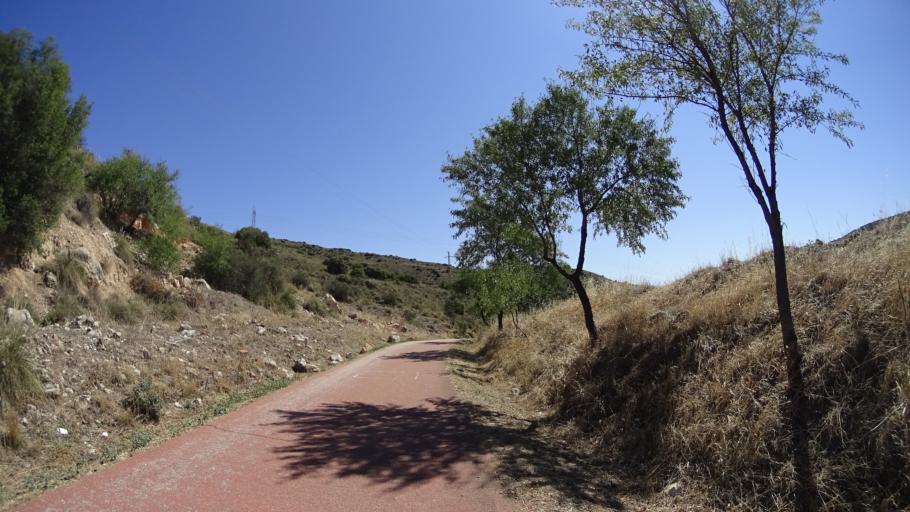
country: ES
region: Madrid
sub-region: Provincia de Madrid
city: Perales de Tajuna
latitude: 40.2324
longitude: -3.3680
